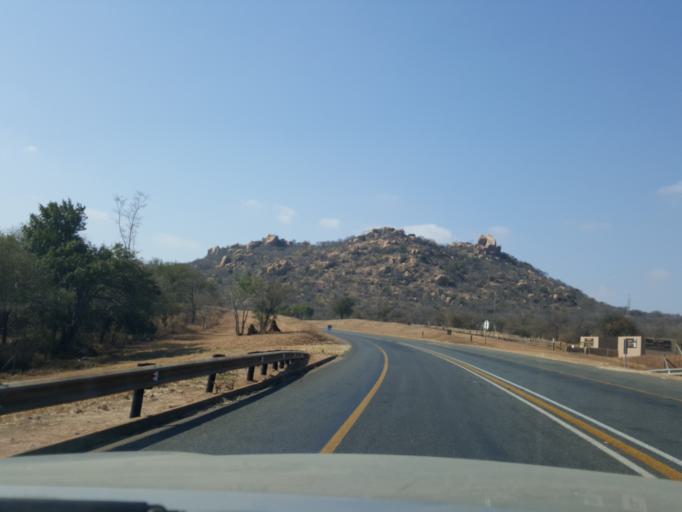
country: ZA
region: Mpumalanga
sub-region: Ehlanzeni District
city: Komatipoort
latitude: -25.4614
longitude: 31.6159
